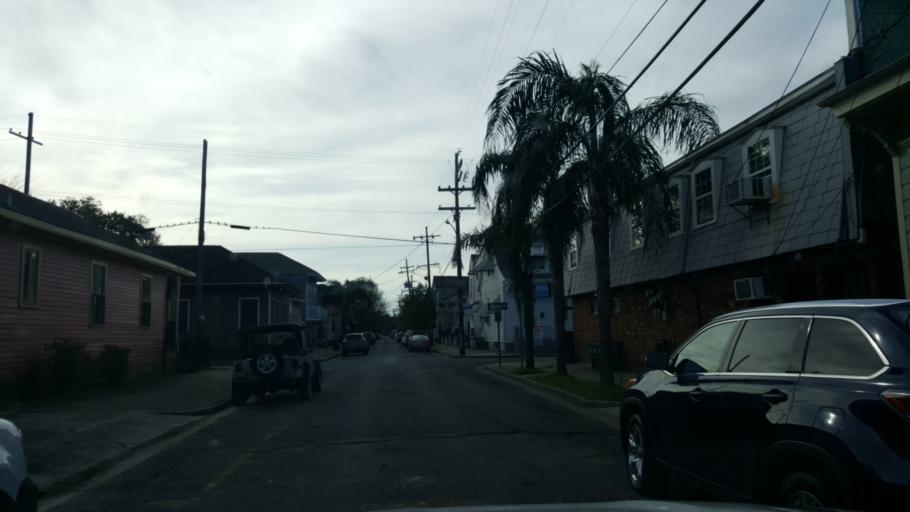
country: US
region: Louisiana
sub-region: Orleans Parish
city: New Orleans
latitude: 29.9679
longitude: -90.0591
